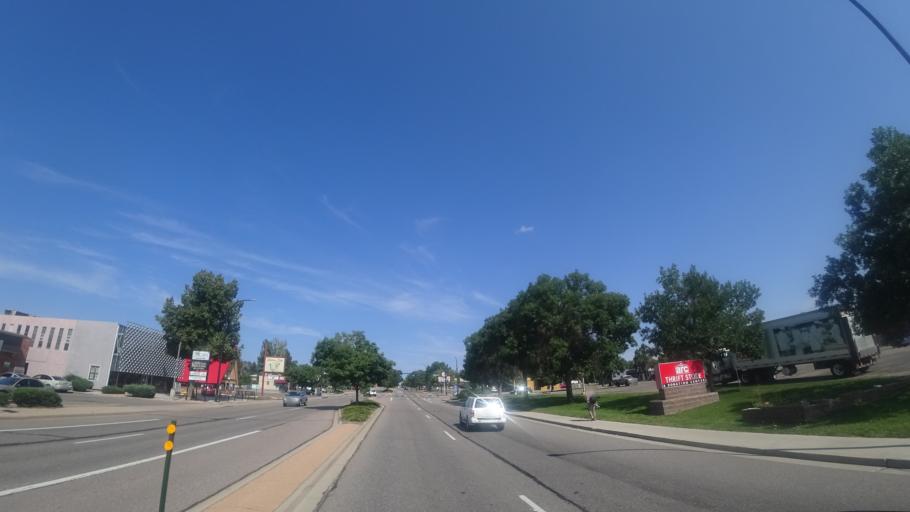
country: US
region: Colorado
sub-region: Arapahoe County
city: Littleton
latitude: 39.6132
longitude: -105.0057
